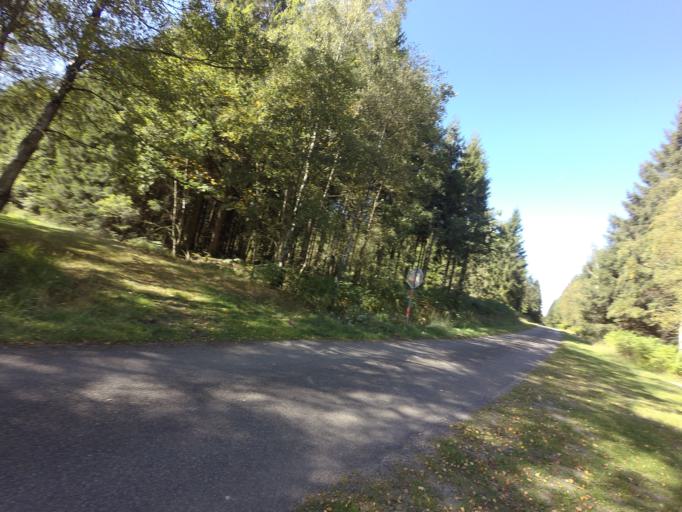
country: DE
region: North Rhine-Westphalia
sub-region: Regierungsbezirk Koln
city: Roetgen
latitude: 50.5986
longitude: 6.1862
